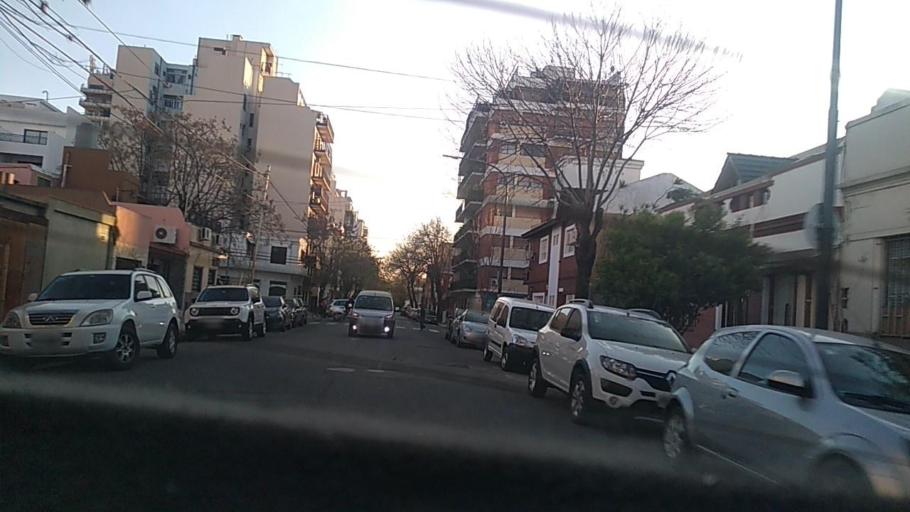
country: AR
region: Buenos Aires F.D.
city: Villa Santa Rita
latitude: -34.6060
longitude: -58.4835
